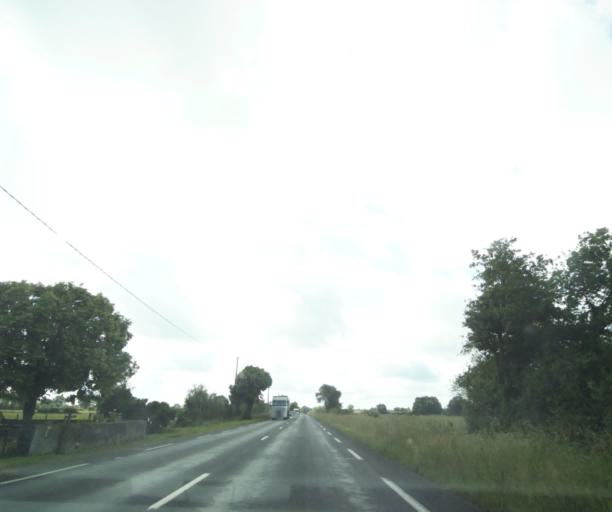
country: FR
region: Pays de la Loire
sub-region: Departement de la Sarthe
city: Vion
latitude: 47.7978
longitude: -0.2612
